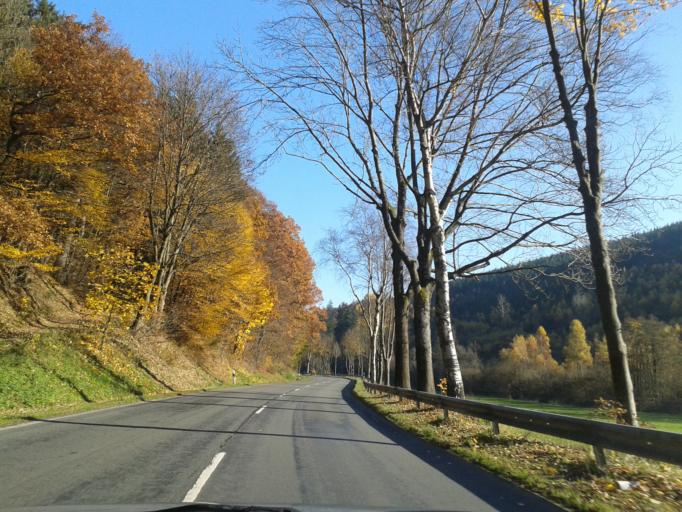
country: DE
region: North Rhine-Westphalia
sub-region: Regierungsbezirk Arnsberg
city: Bad Laasphe
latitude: 50.9240
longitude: 8.3694
